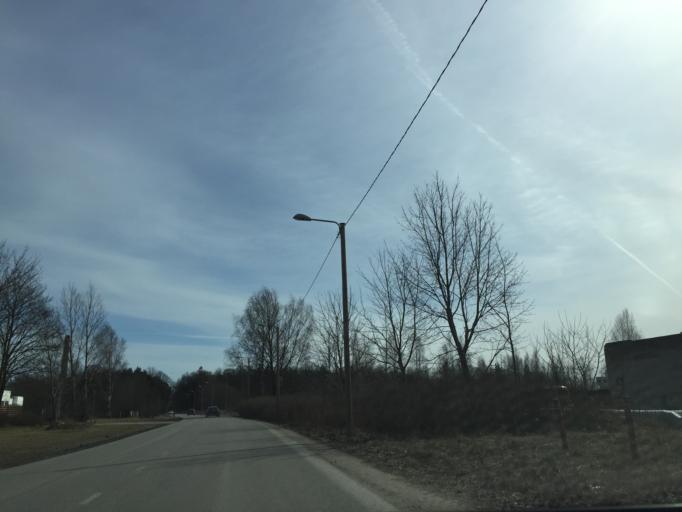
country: EE
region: Paernumaa
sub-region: Paernu linn
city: Parnu
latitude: 58.3806
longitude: 24.5316
